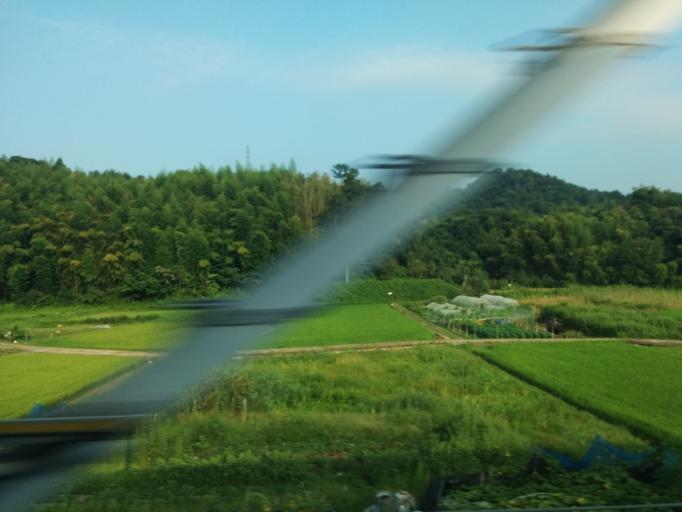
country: JP
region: Shiga Prefecture
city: Hikone
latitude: 35.2702
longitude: 136.2796
